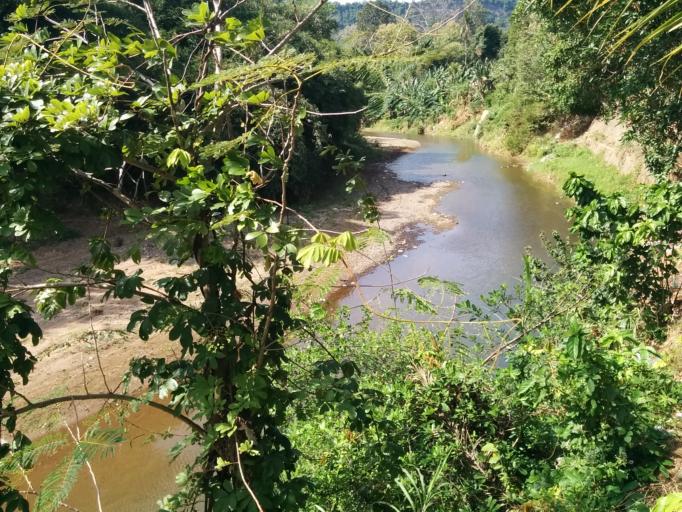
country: ID
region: East Java
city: Sitiarjo
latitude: -8.3773
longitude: 112.6785
